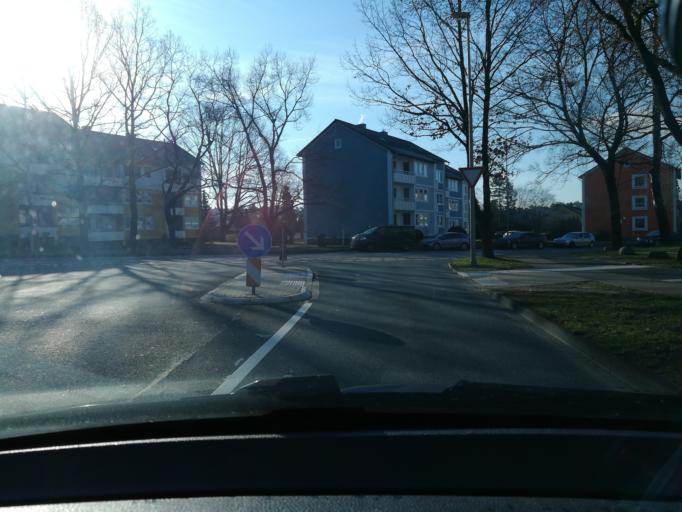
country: DE
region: North Rhine-Westphalia
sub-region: Regierungsbezirk Detmold
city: Oerlinghausen
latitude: 51.9519
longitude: 8.5951
